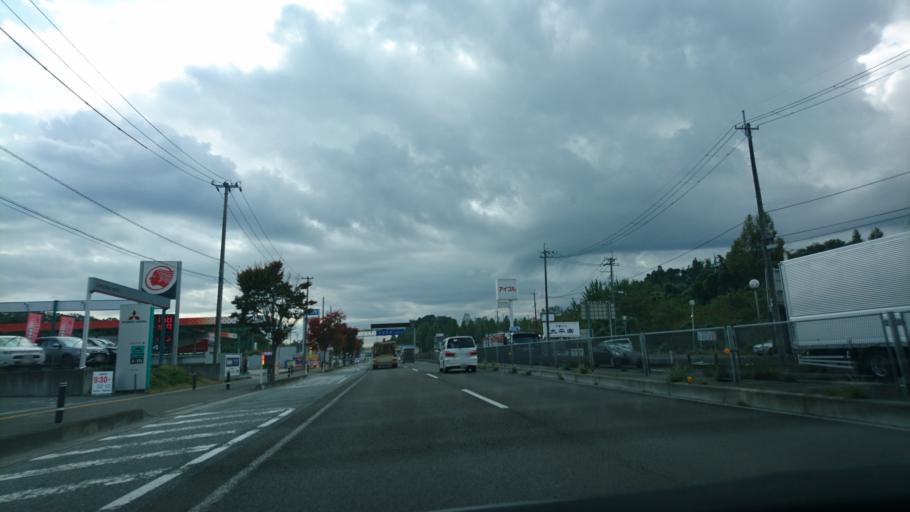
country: JP
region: Miyagi
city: Tomiya
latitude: 38.3480
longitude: 140.8769
